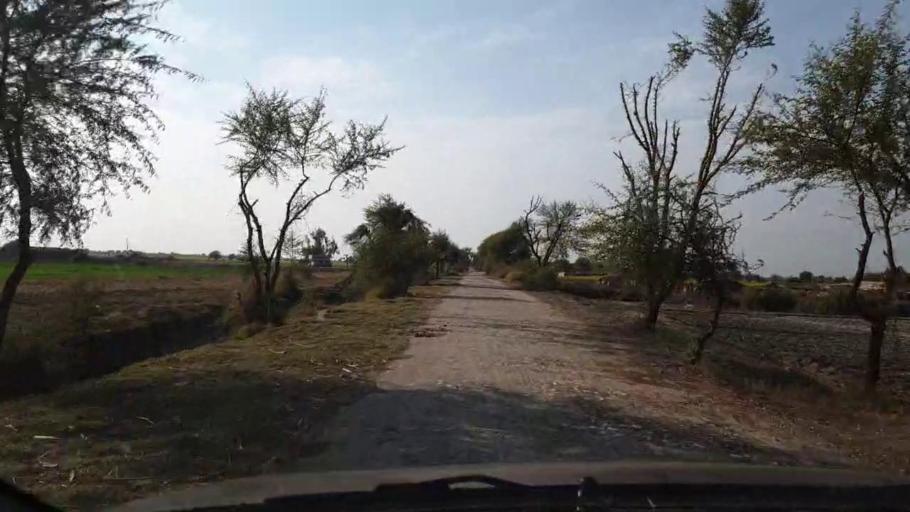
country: PK
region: Sindh
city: Sinjhoro
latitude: 25.9770
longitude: 68.8198
